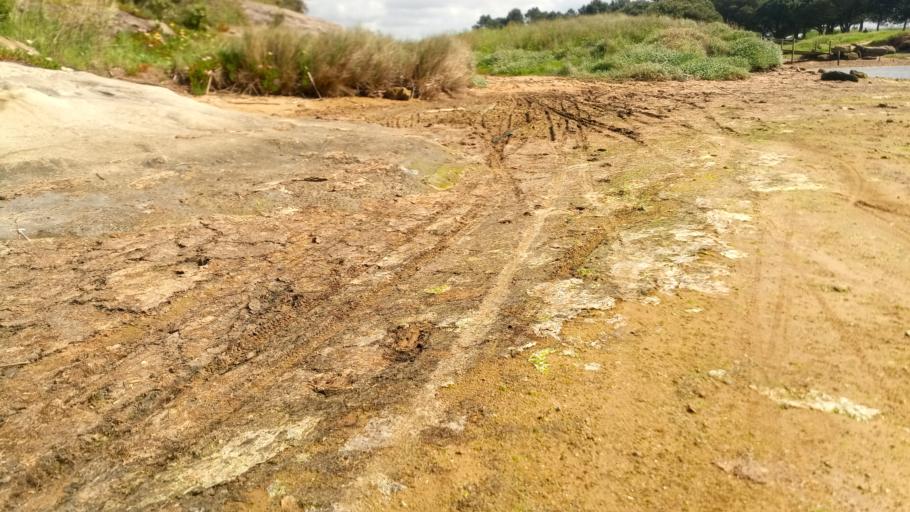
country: PT
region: Leiria
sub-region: Obidos
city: Obidos
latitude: 39.3997
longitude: -9.1981
